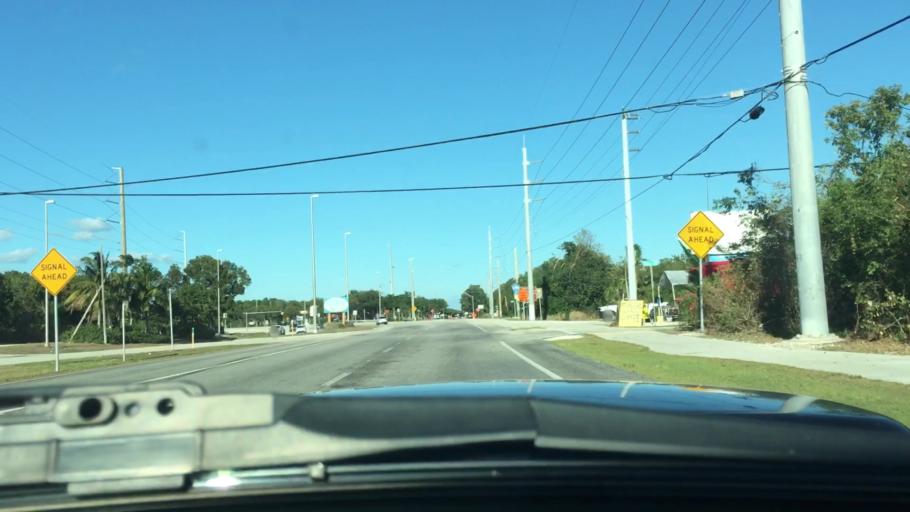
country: US
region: Florida
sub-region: Monroe County
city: Key Largo
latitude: 25.1695
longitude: -80.3754
